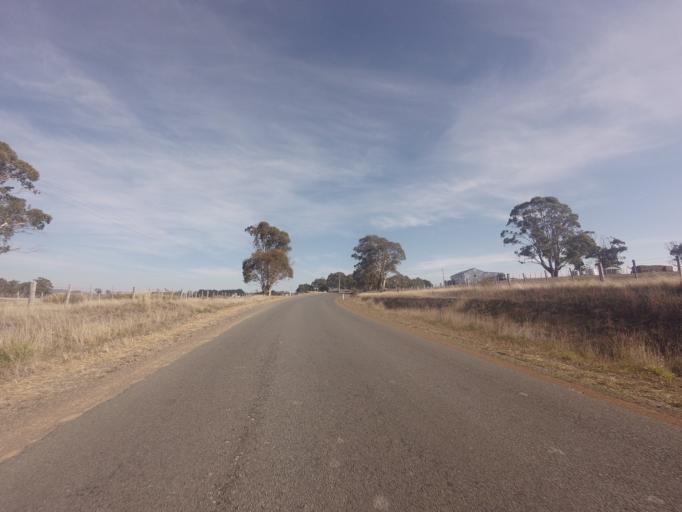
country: AU
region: Tasmania
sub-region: Sorell
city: Sorell
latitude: -42.4456
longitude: 147.4668
